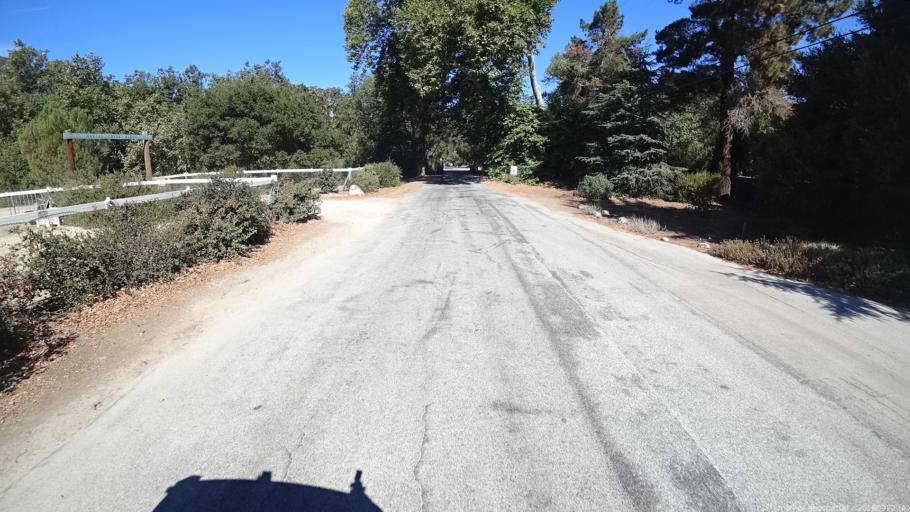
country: US
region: California
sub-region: Monterey County
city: Carmel Valley Village
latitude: 36.4909
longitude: -121.7513
